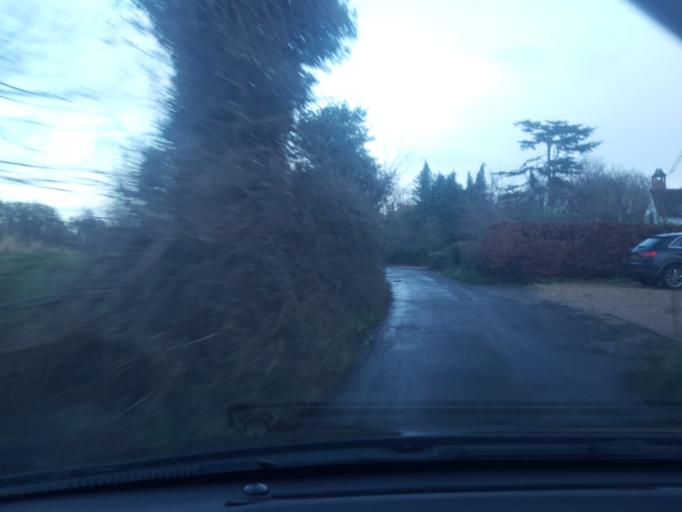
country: GB
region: England
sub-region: Shropshire
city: Albrighton
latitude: 52.6337
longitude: -2.2619
